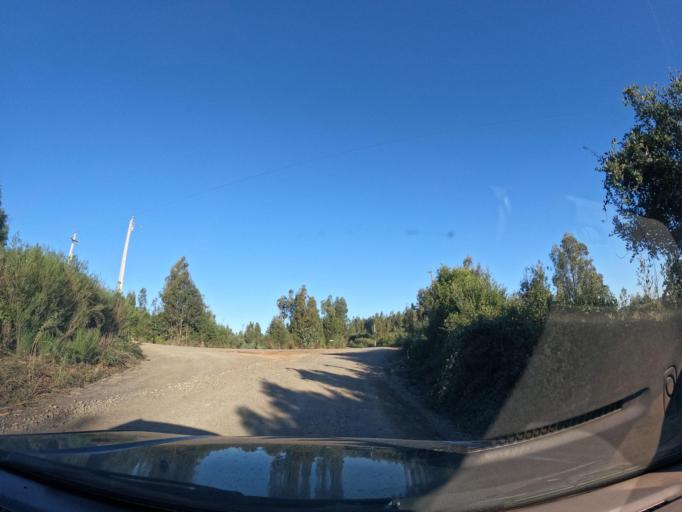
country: CL
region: Biobio
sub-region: Provincia de Concepcion
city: Chiguayante
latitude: -37.0296
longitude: -72.8716
